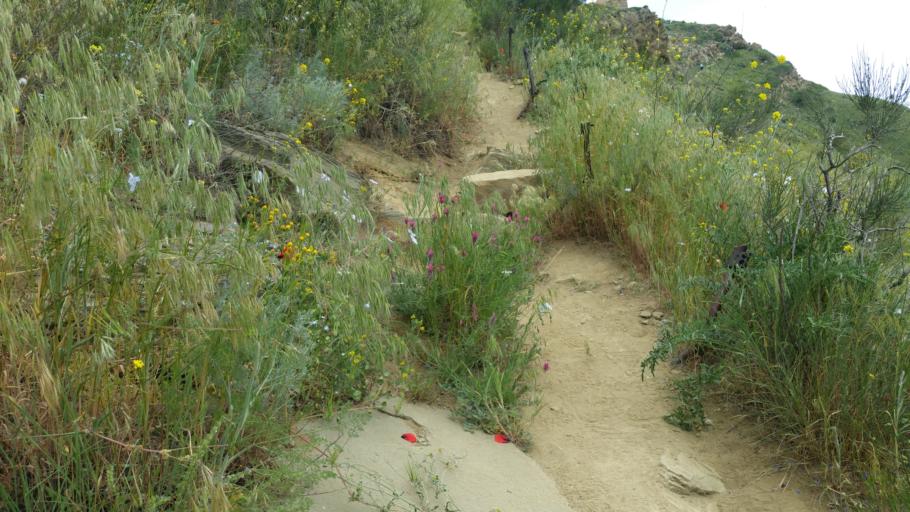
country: AZ
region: Agstafa
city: Saloglu
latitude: 41.4428
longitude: 45.3756
